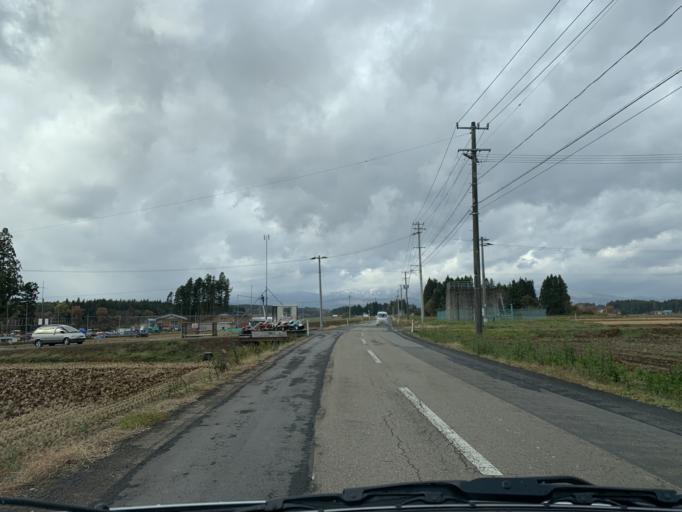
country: JP
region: Iwate
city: Mizusawa
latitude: 39.0800
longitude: 141.0367
